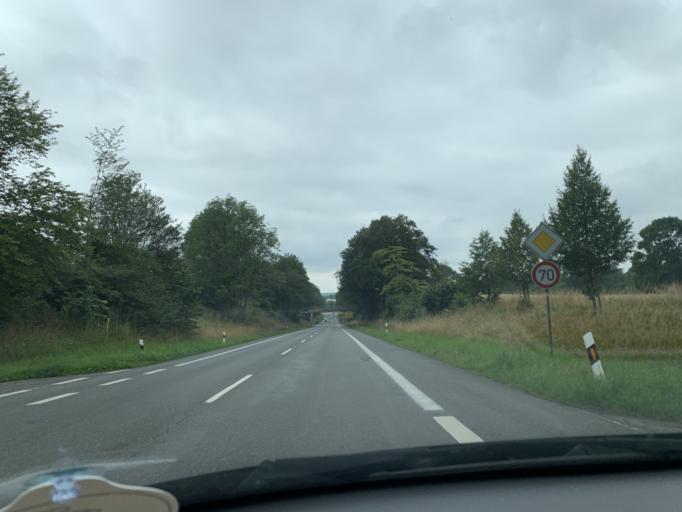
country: DE
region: North Rhine-Westphalia
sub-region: Regierungsbezirk Munster
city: Tecklenburg
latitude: 52.2053
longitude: 7.8262
